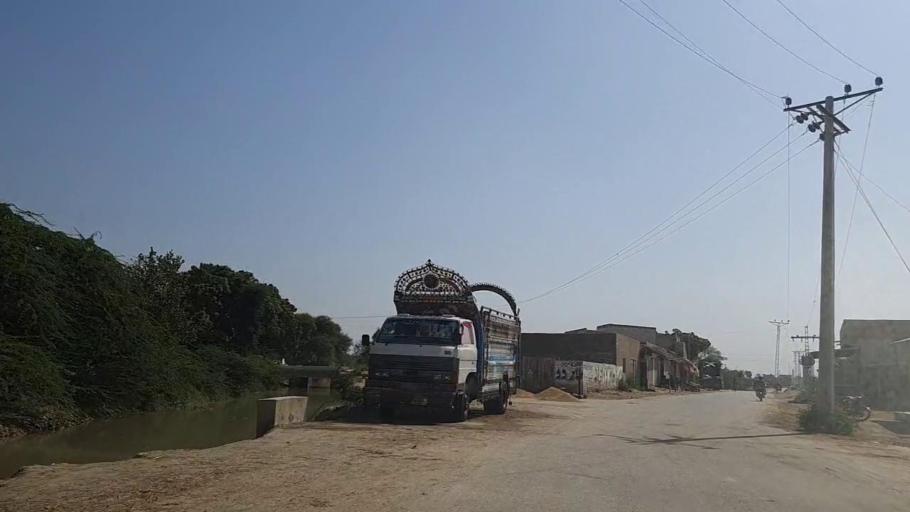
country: PK
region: Sindh
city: Mirpur Batoro
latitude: 24.7365
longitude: 68.2553
